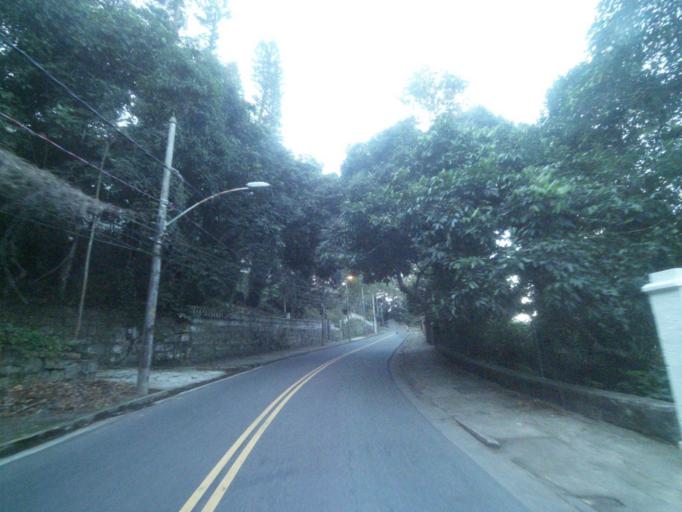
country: BR
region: Rio de Janeiro
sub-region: Rio De Janeiro
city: Rio de Janeiro
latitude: -23.0057
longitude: -43.2830
